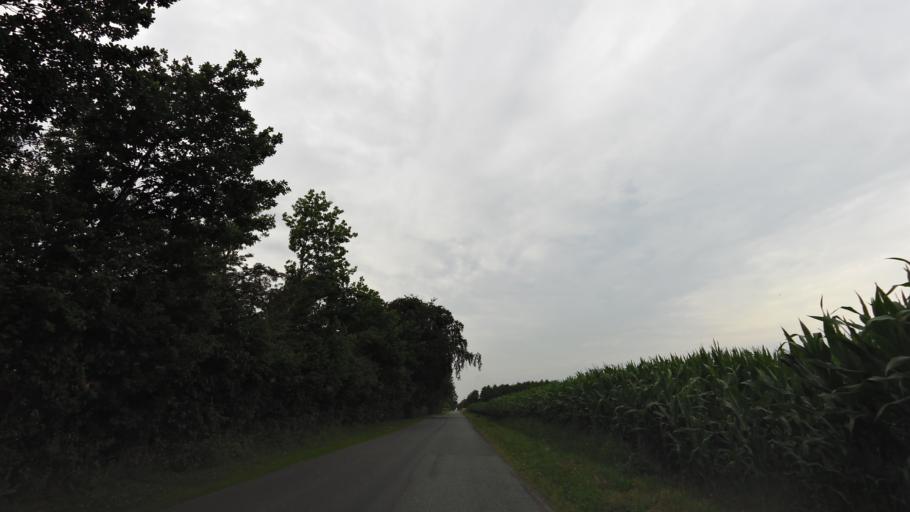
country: DK
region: South Denmark
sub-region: Nordfyns Kommune
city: Otterup
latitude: 55.5688
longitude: 10.4268
